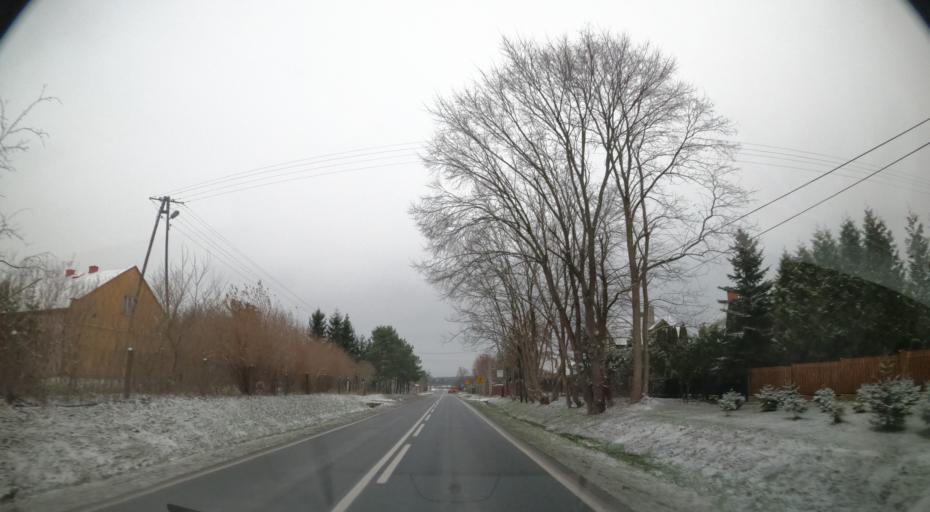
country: PL
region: Masovian Voivodeship
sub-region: Powiat plocki
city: Maszewo Duze
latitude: 52.5720
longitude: 19.5933
